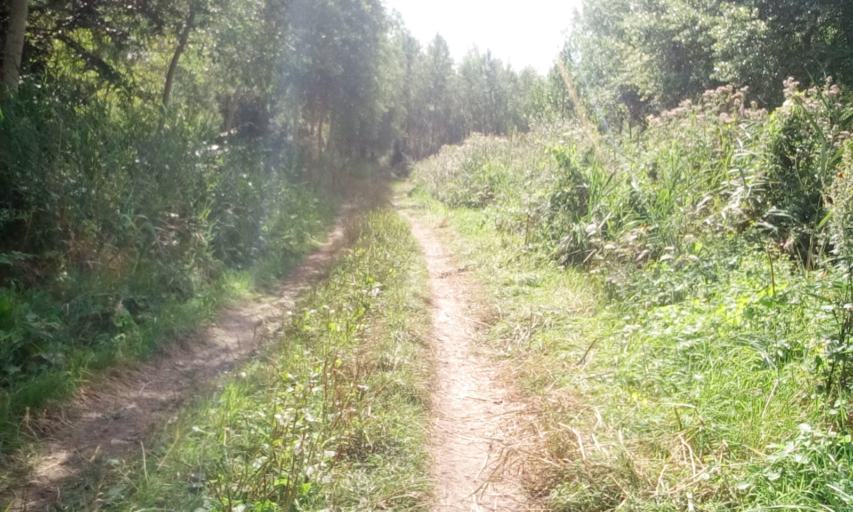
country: FR
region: Lower Normandy
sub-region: Departement du Calvados
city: Argences
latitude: 49.1498
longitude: -0.1690
